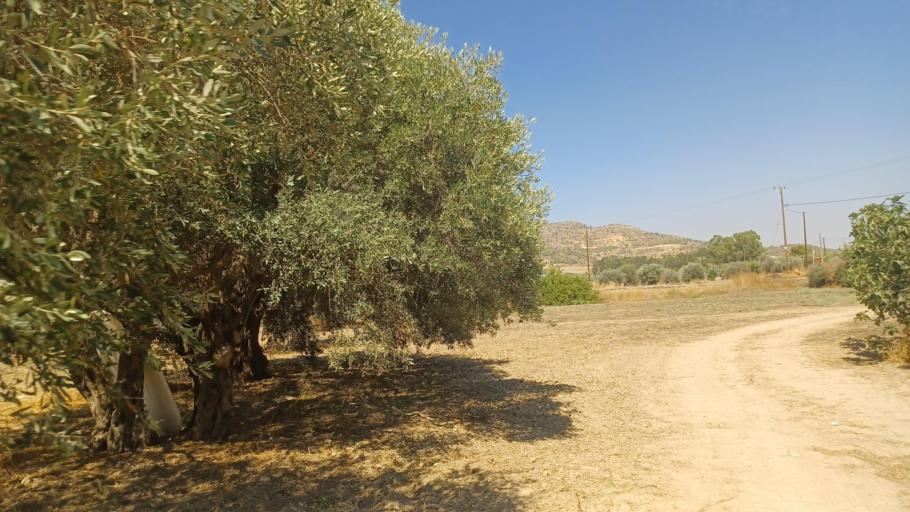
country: CY
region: Larnaka
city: Voroklini
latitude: 34.9984
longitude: 33.6600
